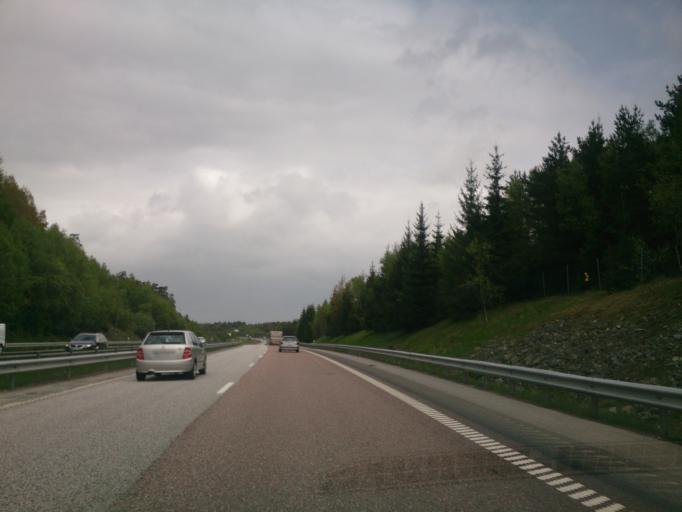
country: SE
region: Stockholm
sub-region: Sodertalje Kommun
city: Pershagen
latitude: 59.1350
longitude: 17.6459
